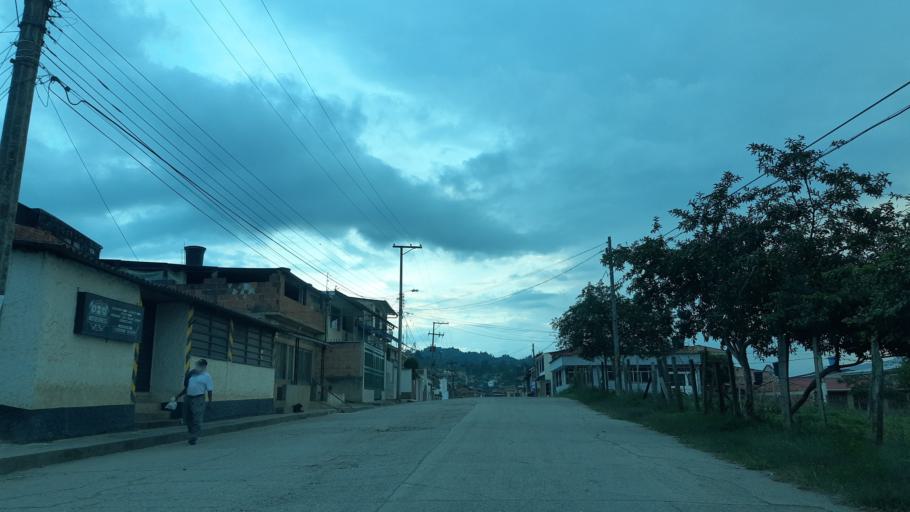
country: CO
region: Boyaca
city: Garagoa
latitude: 5.0870
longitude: -73.3636
